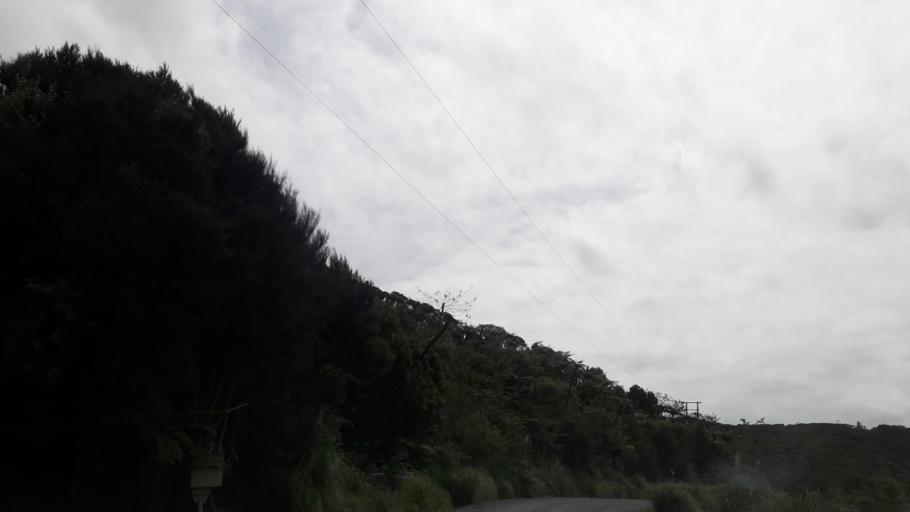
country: NZ
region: Northland
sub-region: Far North District
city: Taipa
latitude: -35.0247
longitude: 173.5523
